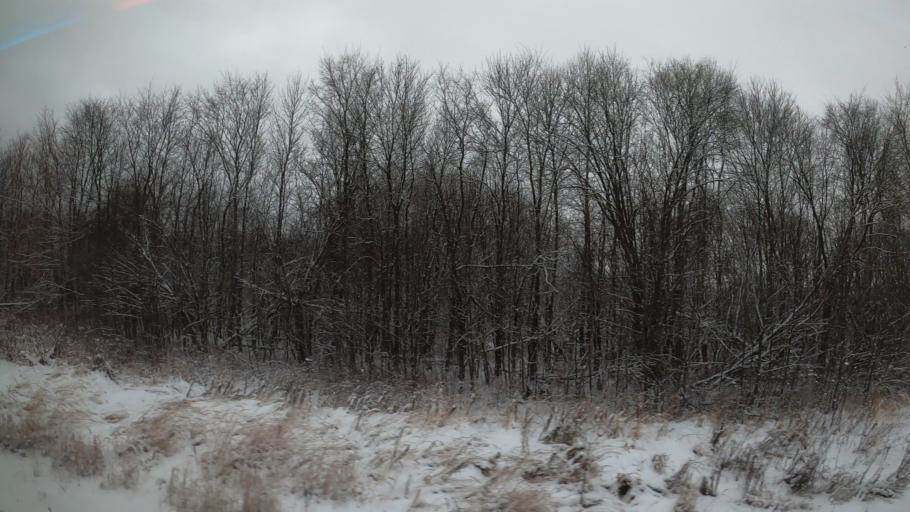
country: RU
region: Jaroslavl
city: Pereslavl'-Zalesskiy
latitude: 56.6917
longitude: 38.9151
